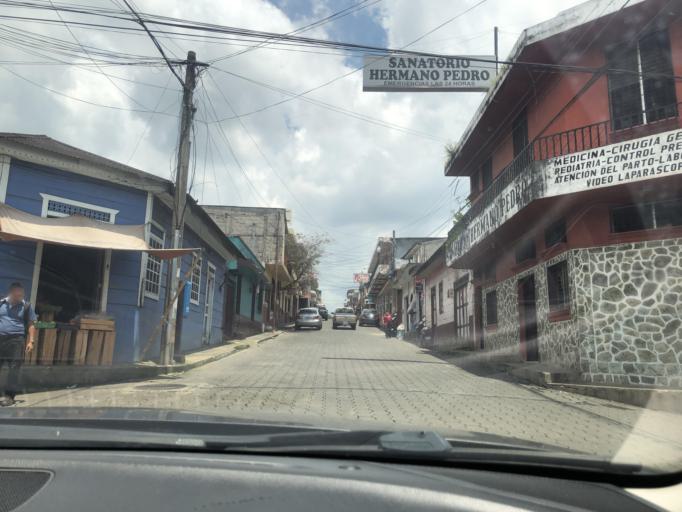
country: GT
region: Quetzaltenango
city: Coatepeque
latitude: 14.7034
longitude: -91.8679
